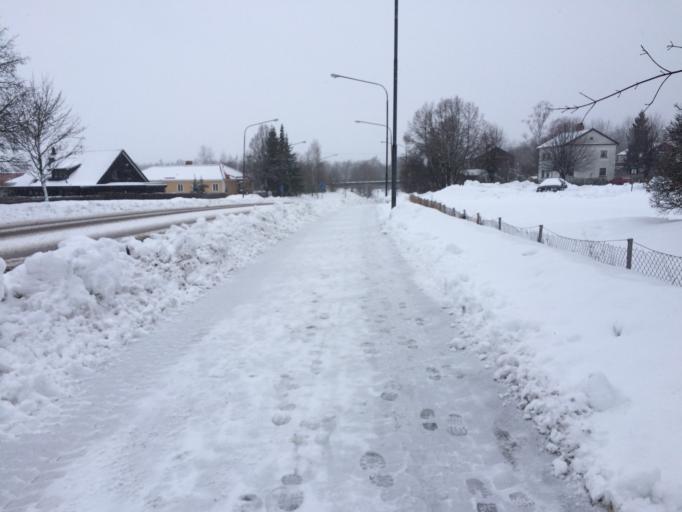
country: SE
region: Vaestmanland
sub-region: Hallstahammars Kommun
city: Hallstahammar
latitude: 59.6109
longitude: 16.2289
